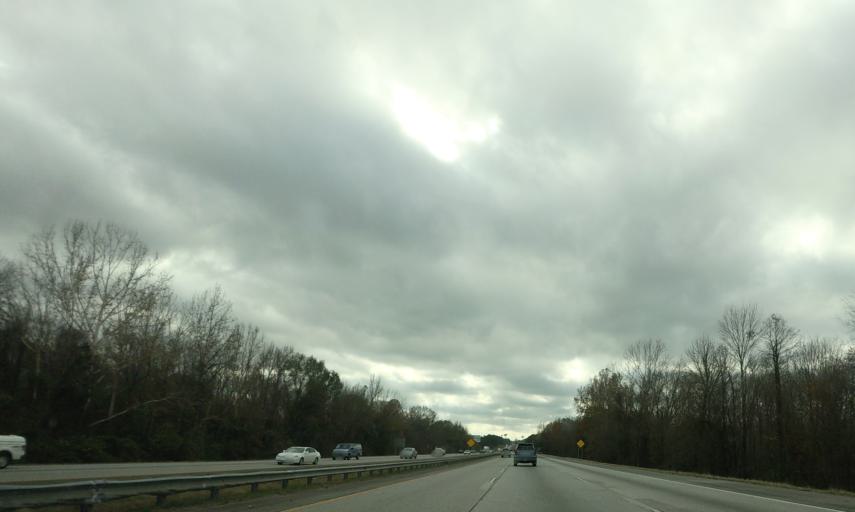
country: US
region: Georgia
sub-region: Peach County
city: Byron
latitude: 32.6981
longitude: -83.7364
